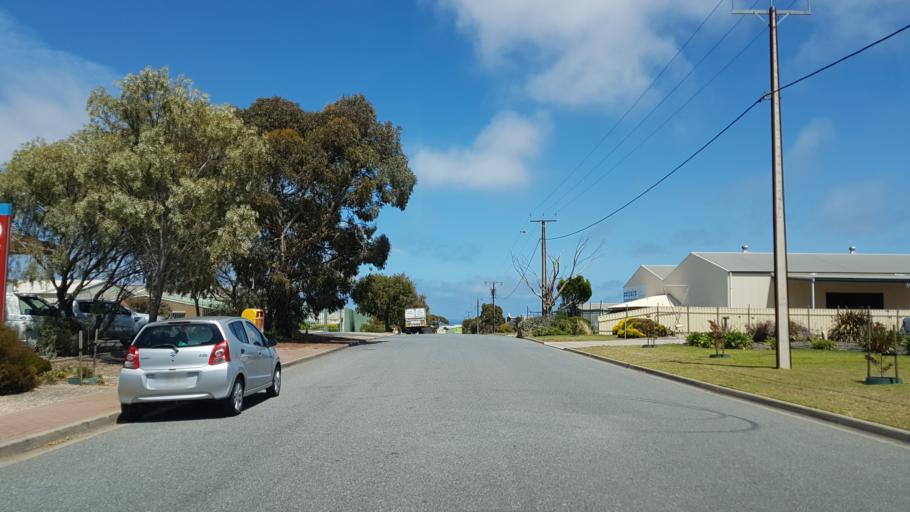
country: AU
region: South Australia
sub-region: Onkaparinga
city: Morphett Vale
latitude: -35.1149
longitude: 138.5048
